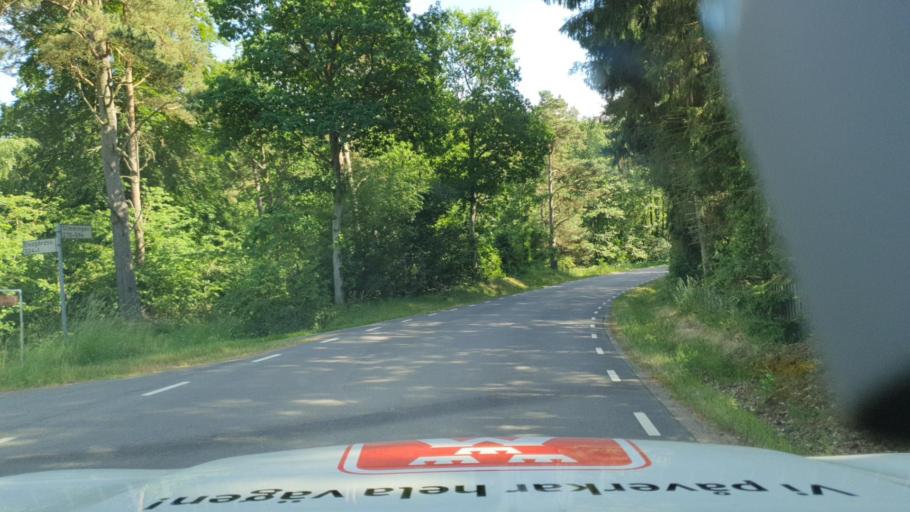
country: SE
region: Skane
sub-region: Sjobo Kommun
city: Blentarp
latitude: 55.5653
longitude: 13.5737
